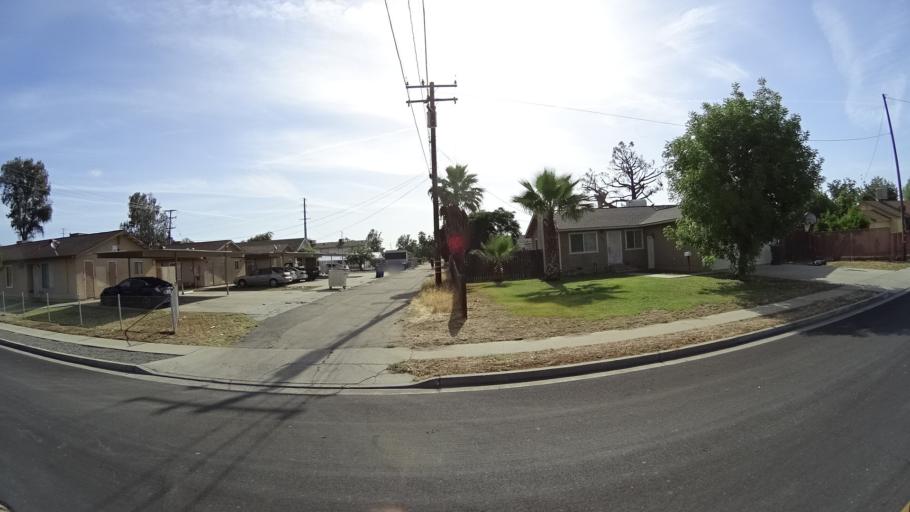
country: US
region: California
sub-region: Kings County
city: Hanford
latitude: 36.3212
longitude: -119.6495
